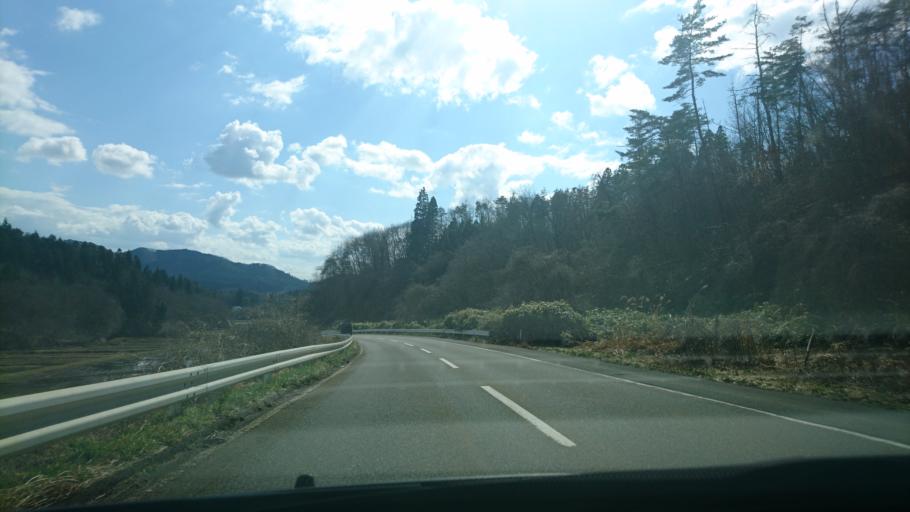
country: JP
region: Iwate
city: Kitakami
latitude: 39.3067
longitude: 141.2061
